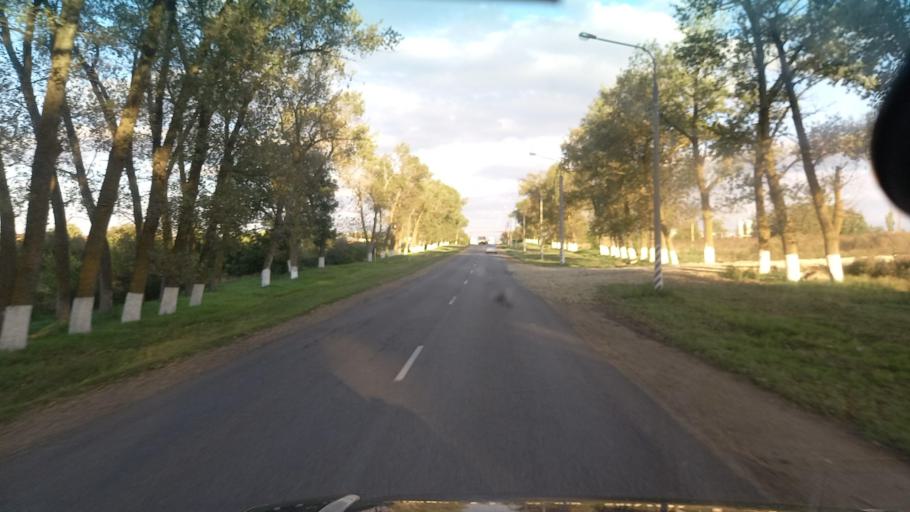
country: RU
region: Krasnodarskiy
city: Krymsk
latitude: 44.9392
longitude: 37.9401
